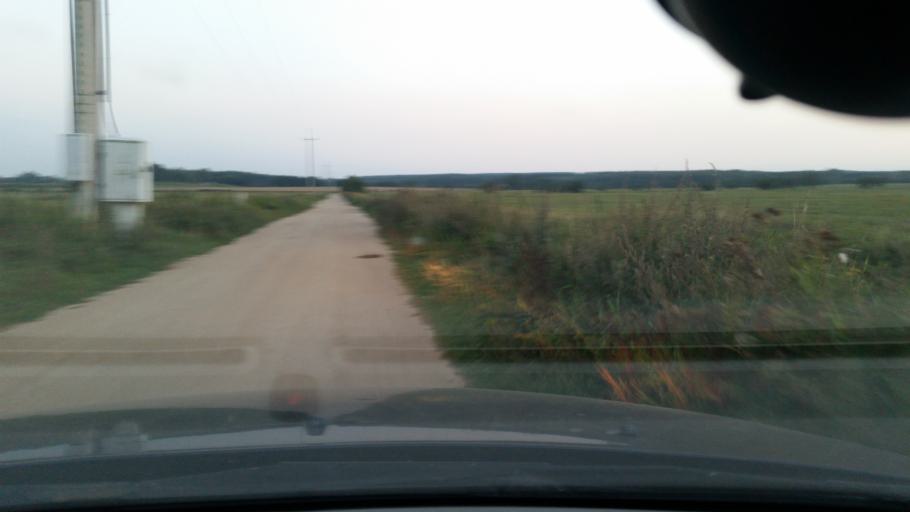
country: PL
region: Pomeranian Voivodeship
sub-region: Powiat wejherowski
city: Choczewo
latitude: 54.7807
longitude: 17.7931
